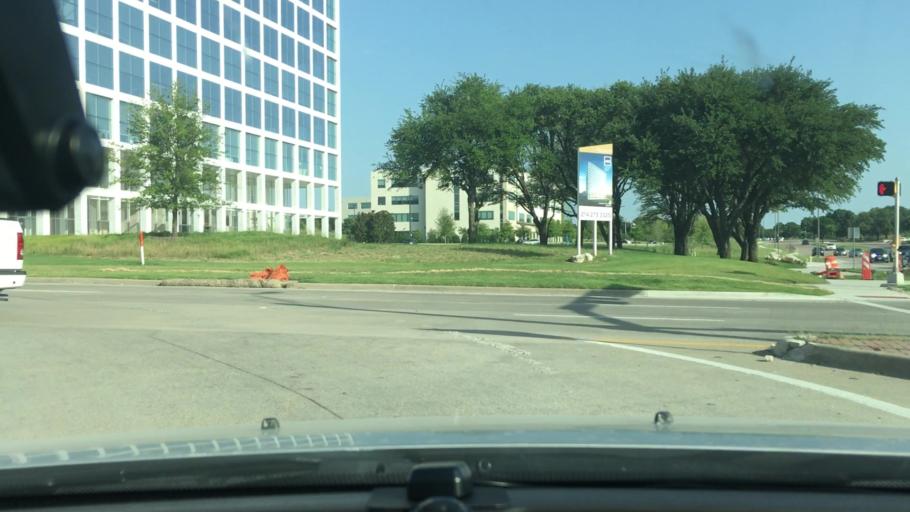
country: US
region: Texas
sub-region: Denton County
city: The Colony
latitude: 33.0863
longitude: -96.8385
